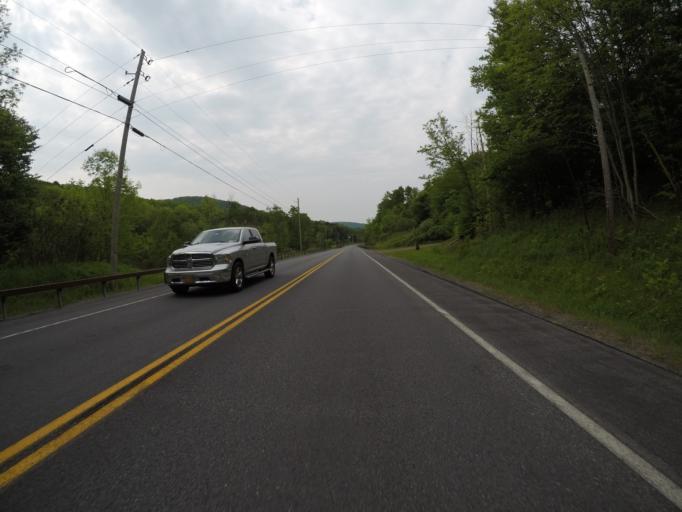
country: US
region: New York
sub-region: Sullivan County
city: Livingston Manor
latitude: 42.0158
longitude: -74.8902
